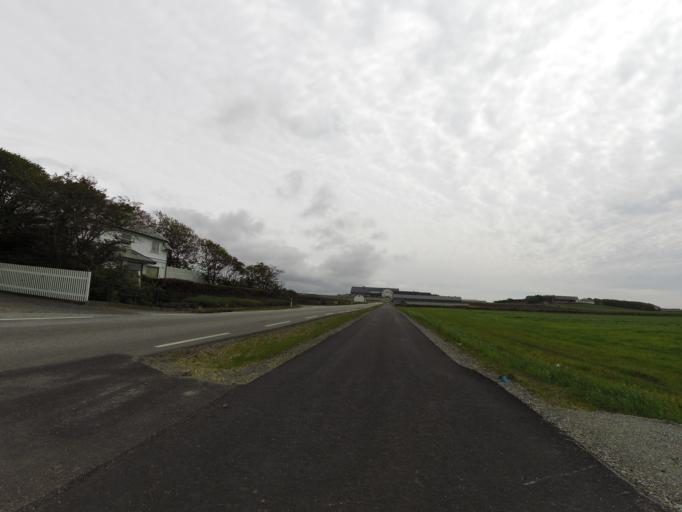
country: NO
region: Rogaland
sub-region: Ha
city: Naerbo
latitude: 58.6831
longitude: 5.5646
